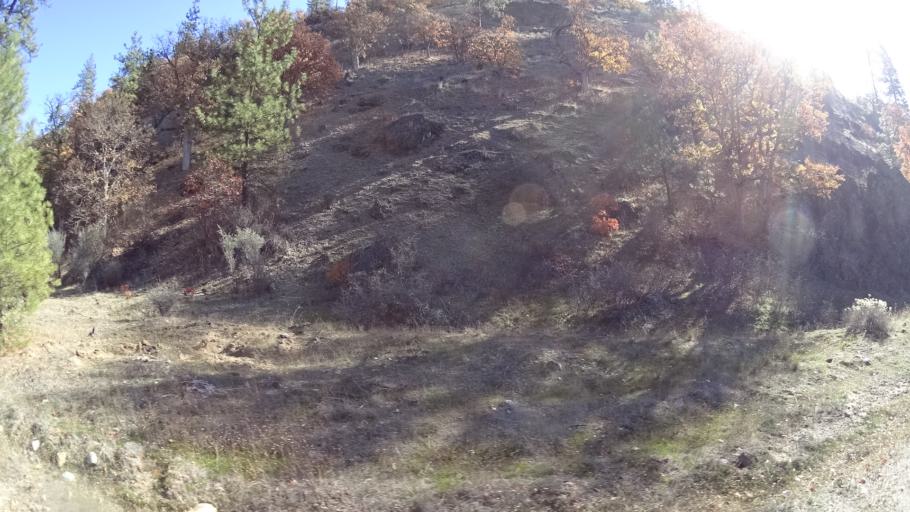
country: US
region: California
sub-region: Siskiyou County
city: Yreka
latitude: 41.8669
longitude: -122.8172
